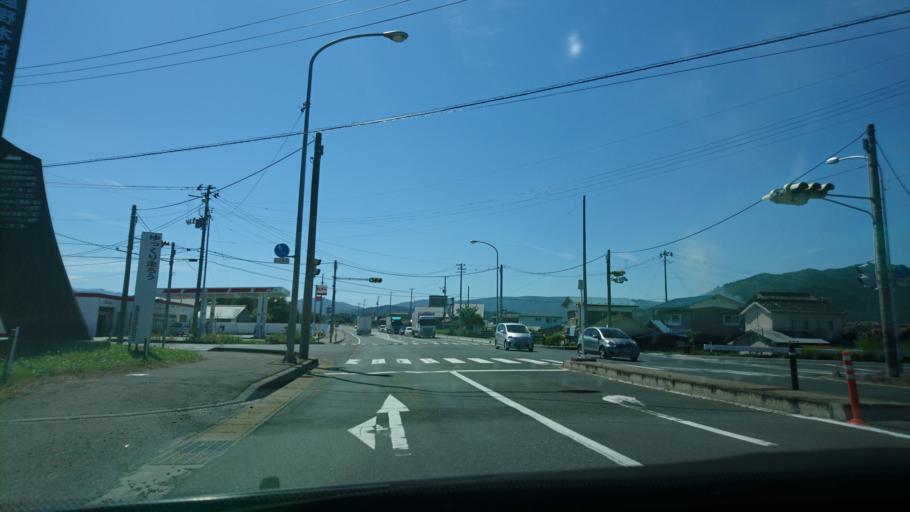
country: JP
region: Iwate
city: Tono
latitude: 39.3123
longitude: 141.5701
